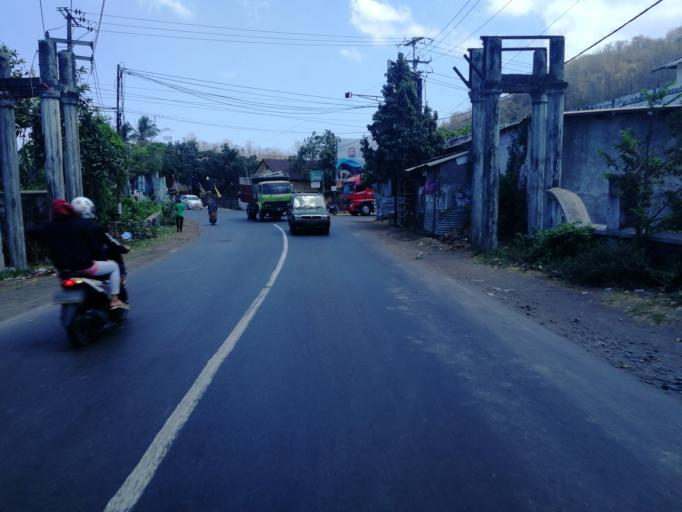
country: ID
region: West Nusa Tenggara
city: Jelateng Timur
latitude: -8.7222
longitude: 116.0758
